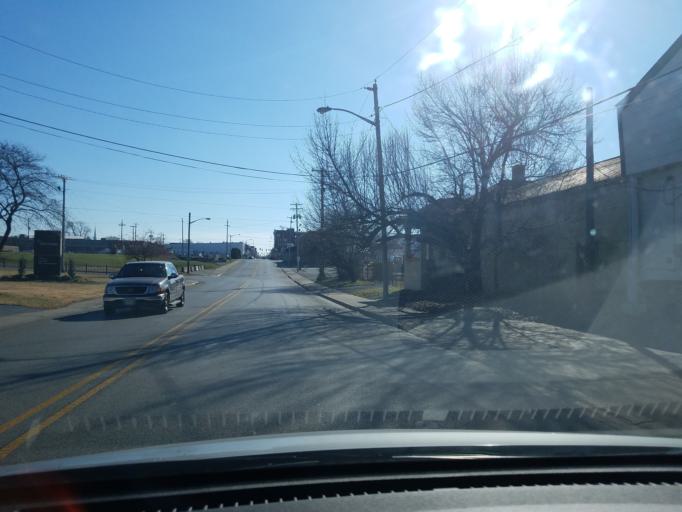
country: US
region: Indiana
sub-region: Floyd County
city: New Albany
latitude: 38.2898
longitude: -85.8250
